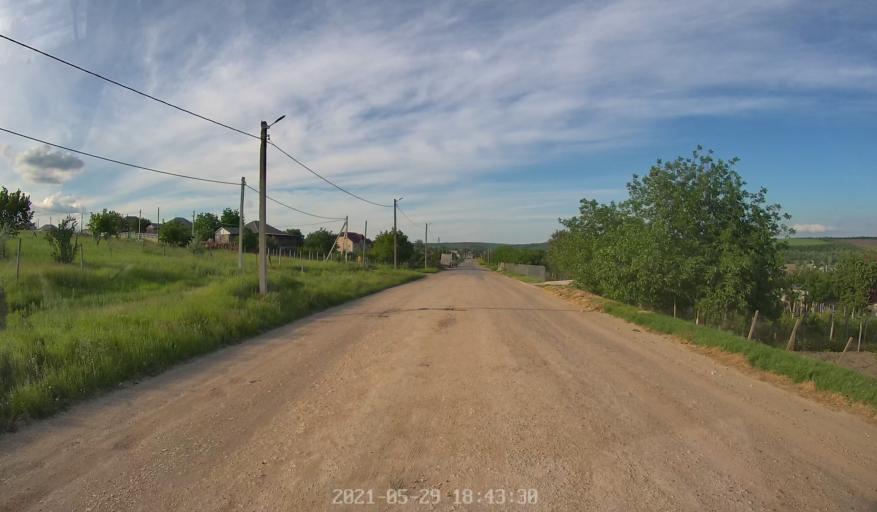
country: MD
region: Chisinau
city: Singera
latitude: 46.8189
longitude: 28.9649
